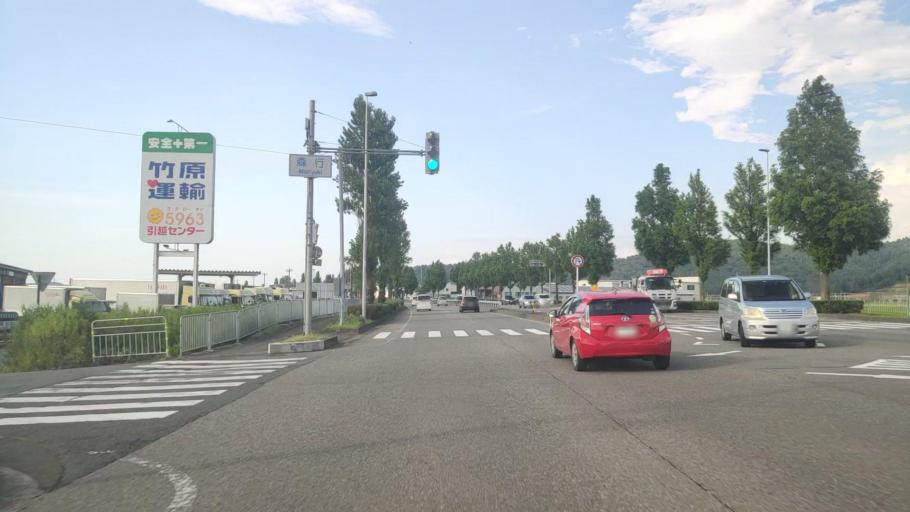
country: JP
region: Fukui
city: Sabae
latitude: 35.9933
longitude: 136.2043
